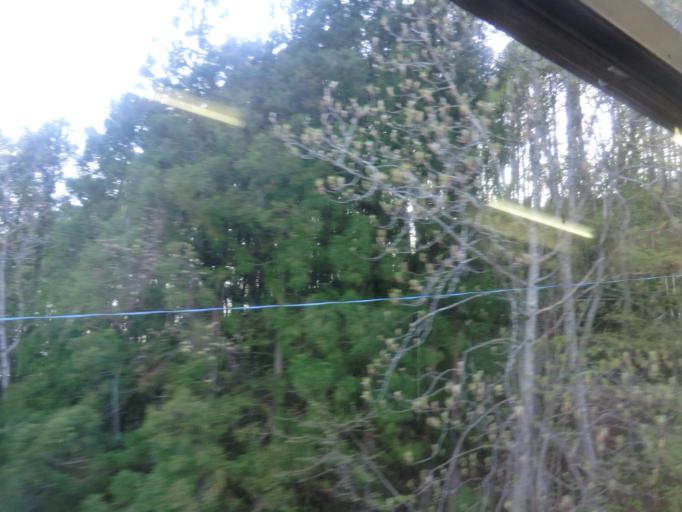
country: JP
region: Iwate
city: Miyako
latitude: 40.0515
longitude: 141.8601
